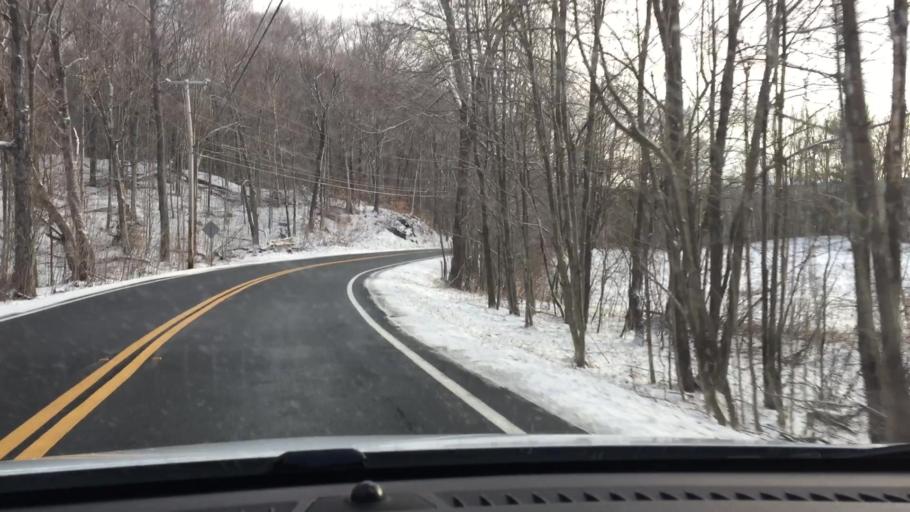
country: US
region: Massachusetts
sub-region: Berkshire County
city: Hinsdale
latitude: 42.4097
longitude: -73.1216
